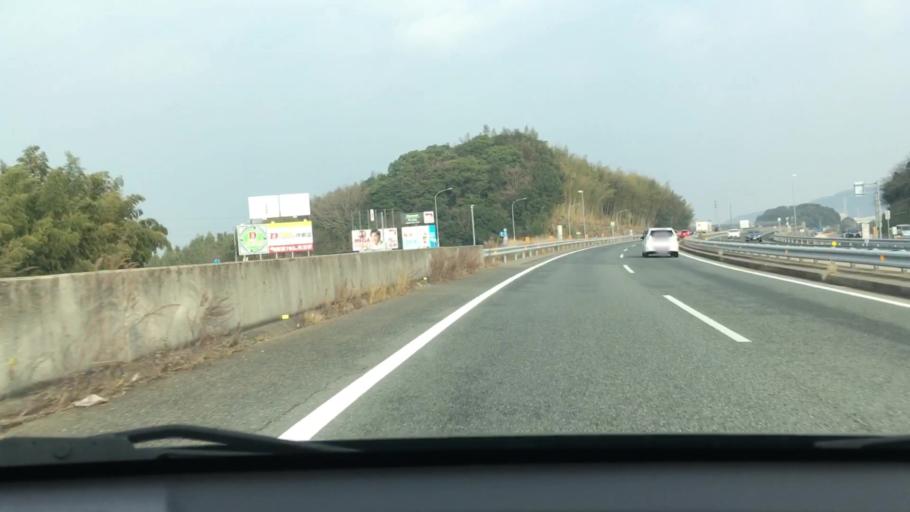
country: JP
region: Fukuoka
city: Maebaru-chuo
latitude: 33.5722
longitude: 130.2514
